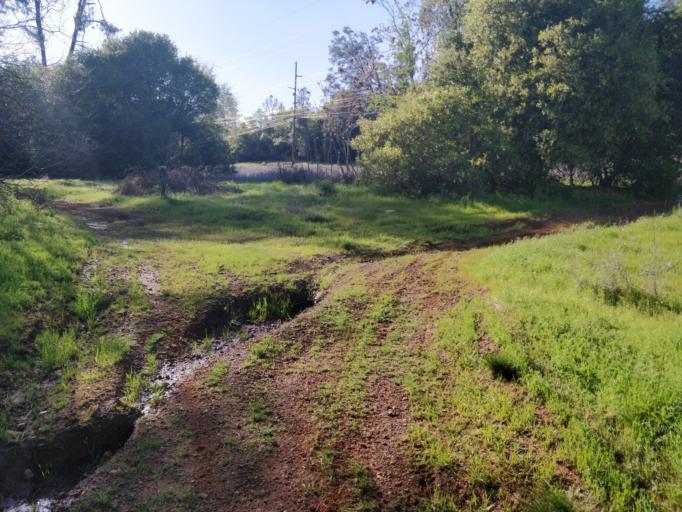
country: US
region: California
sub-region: Shasta County
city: Shasta Lake
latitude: 40.6684
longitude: -122.3688
